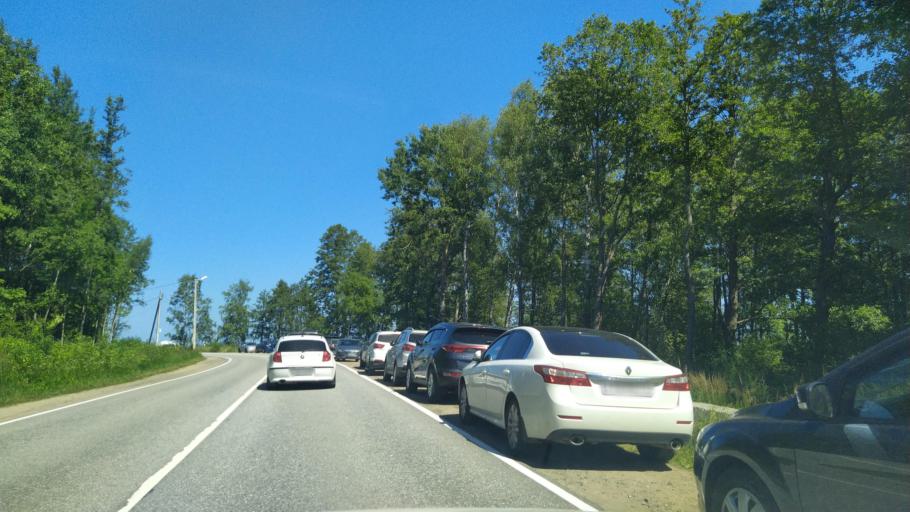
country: RU
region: Leningrad
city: Borisova Griva
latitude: 60.1117
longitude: 31.0843
